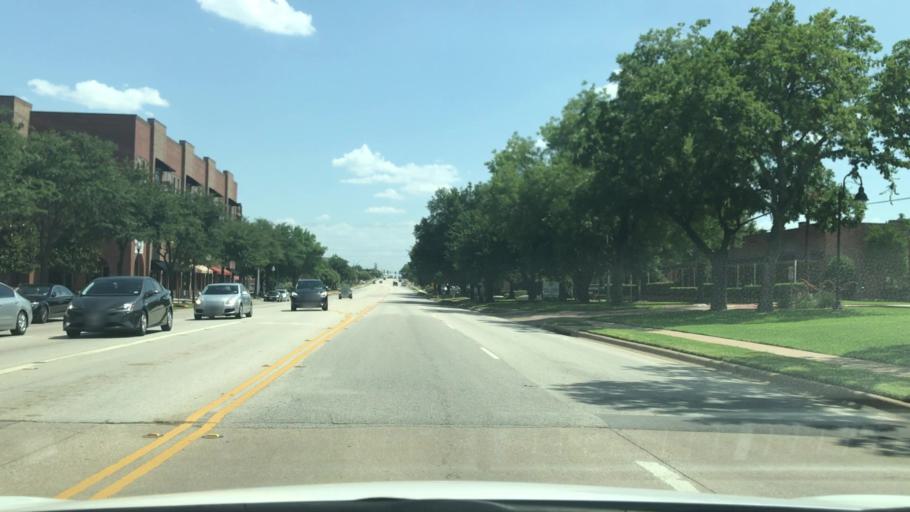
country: US
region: Texas
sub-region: Tarrant County
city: Grapevine
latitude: 32.9326
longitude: -97.0784
